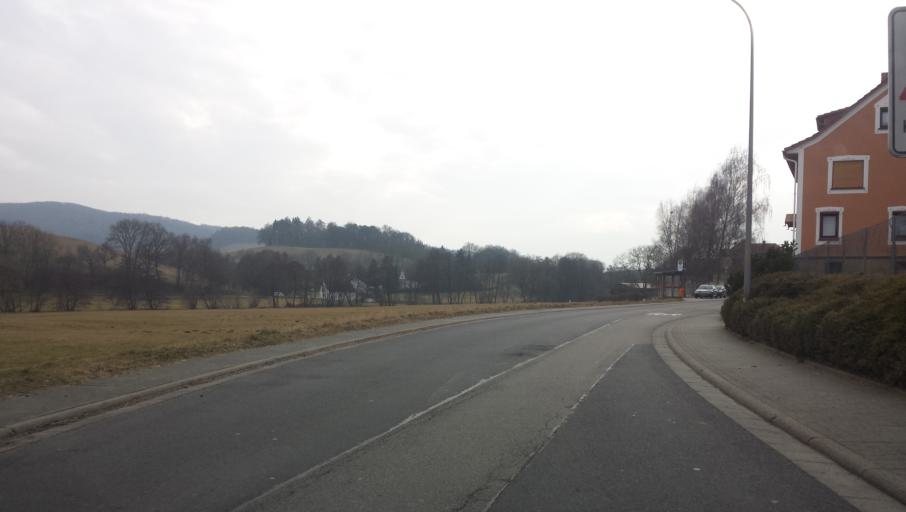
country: DE
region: Hesse
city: Reichelsheim
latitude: 49.7035
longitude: 8.8239
